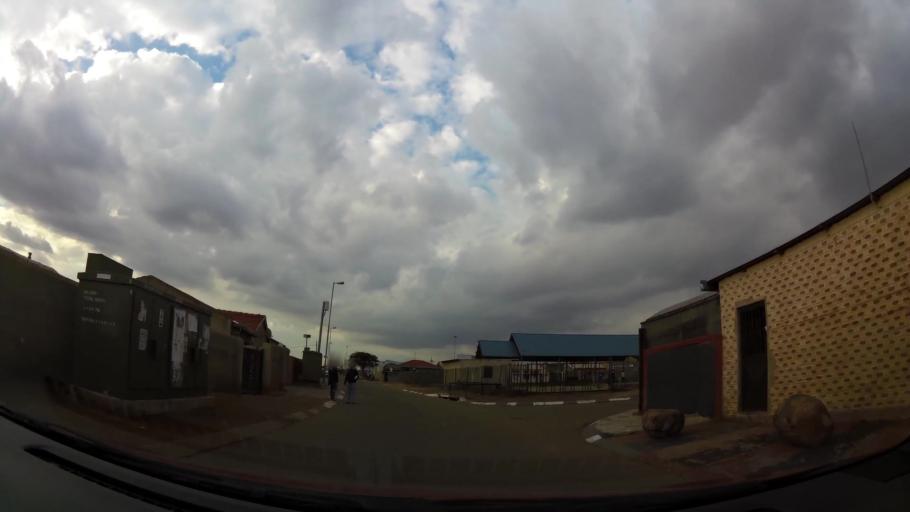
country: ZA
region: Gauteng
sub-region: City of Johannesburg Metropolitan Municipality
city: Soweto
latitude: -26.2405
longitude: 27.8212
